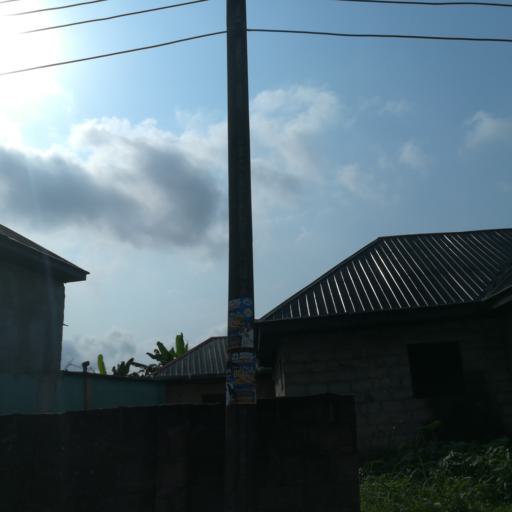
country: NG
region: Rivers
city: Okrika
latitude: 4.7794
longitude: 7.1356
